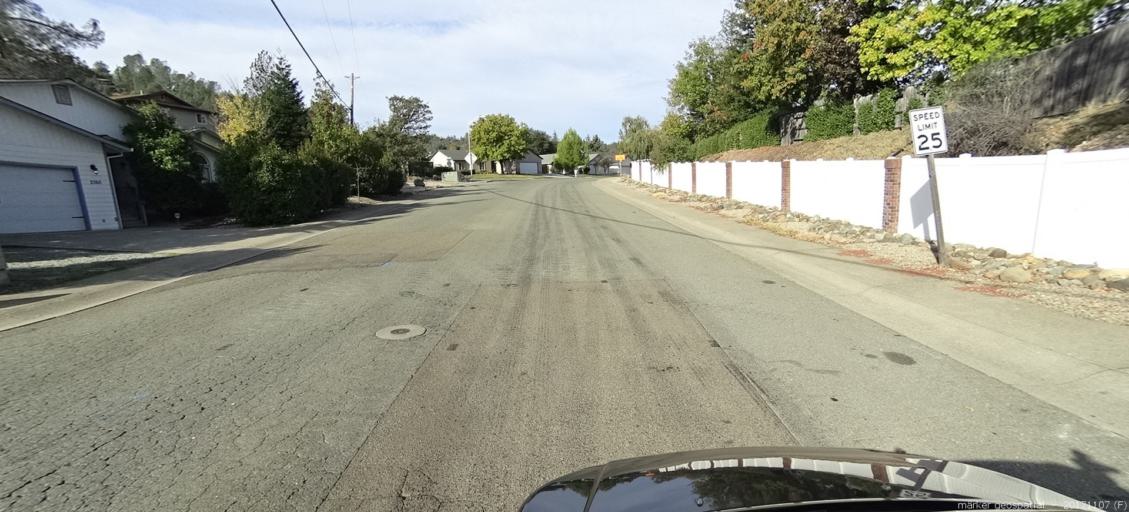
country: US
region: California
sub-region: Shasta County
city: Redding
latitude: 40.5669
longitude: -122.4316
